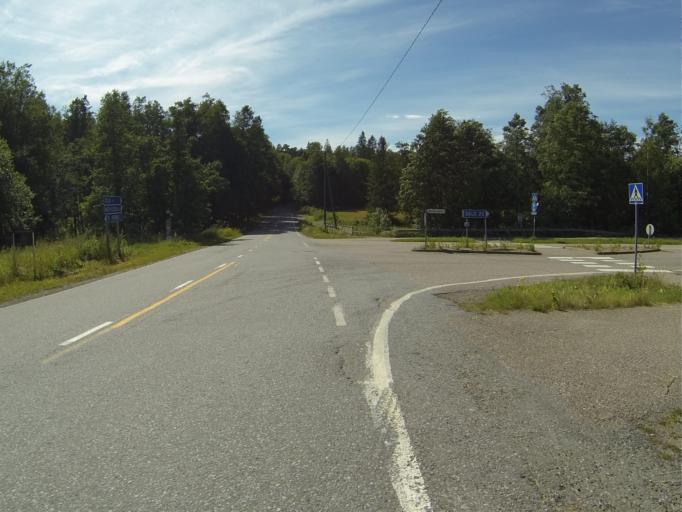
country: FI
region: Varsinais-Suomi
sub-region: Salo
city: Saerkisalo
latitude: 60.2552
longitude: 22.9668
